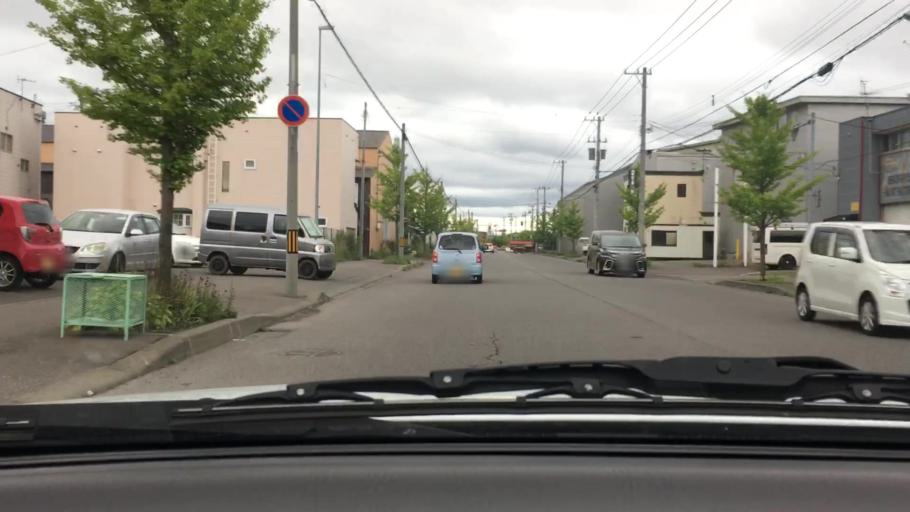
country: JP
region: Hokkaido
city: Hakodate
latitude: 41.7987
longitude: 140.7243
